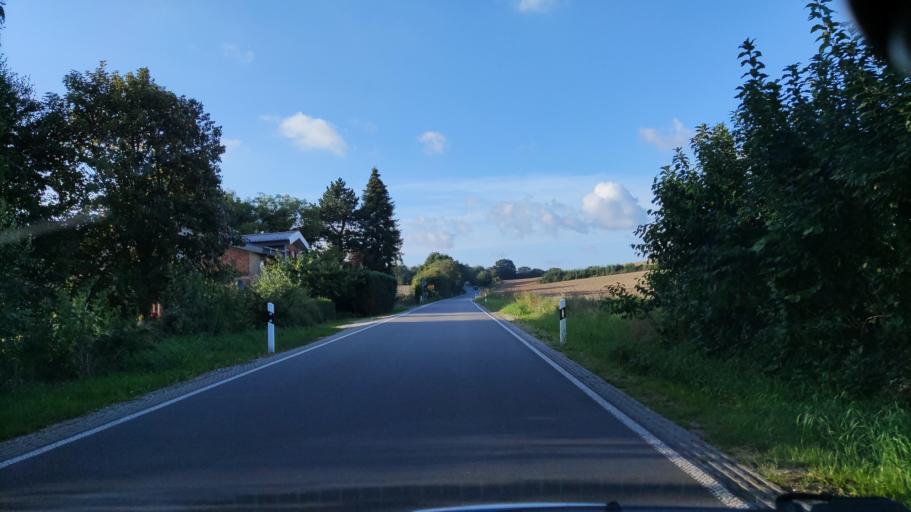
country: DE
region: Schleswig-Holstein
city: Bosdorf
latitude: 54.1011
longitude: 10.4799
